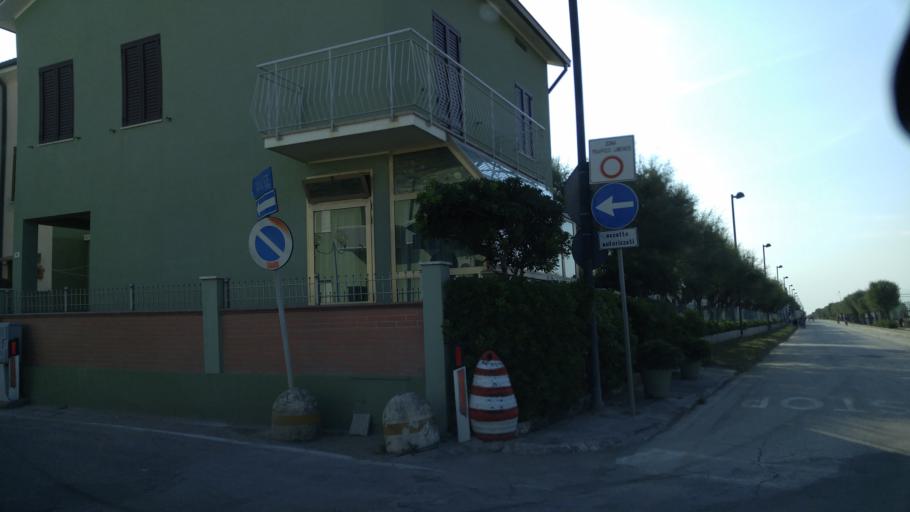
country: IT
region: The Marches
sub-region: Provincia di Pesaro e Urbino
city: Marotta
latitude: 43.7798
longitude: 13.1235
